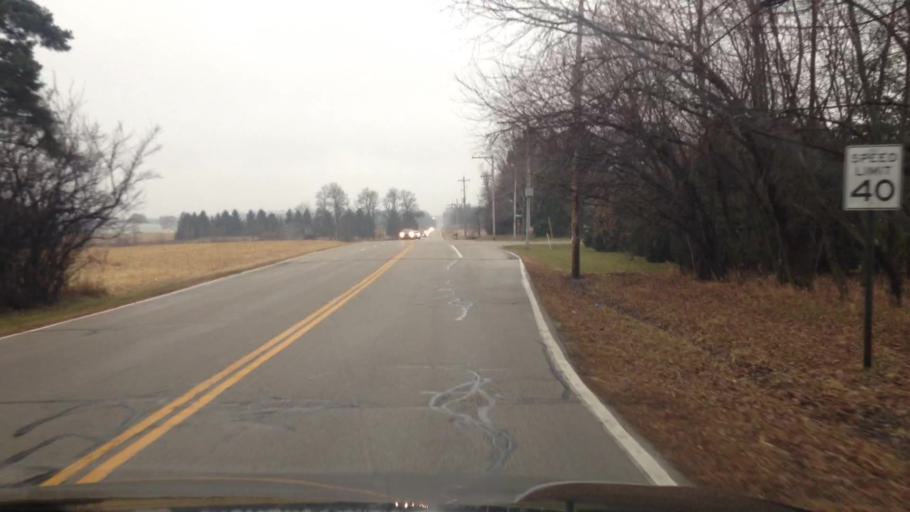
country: US
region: Wisconsin
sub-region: Washington County
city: Germantown
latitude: 43.2493
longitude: -88.1430
